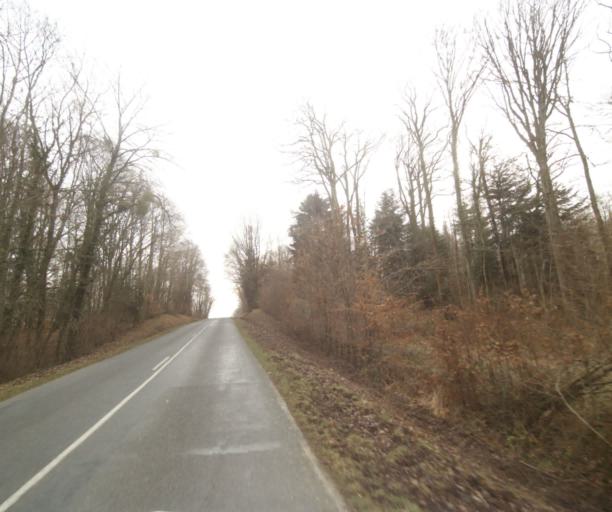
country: FR
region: Champagne-Ardenne
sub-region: Departement de la Haute-Marne
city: Villiers-en-Lieu
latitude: 48.7173
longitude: 4.8802
